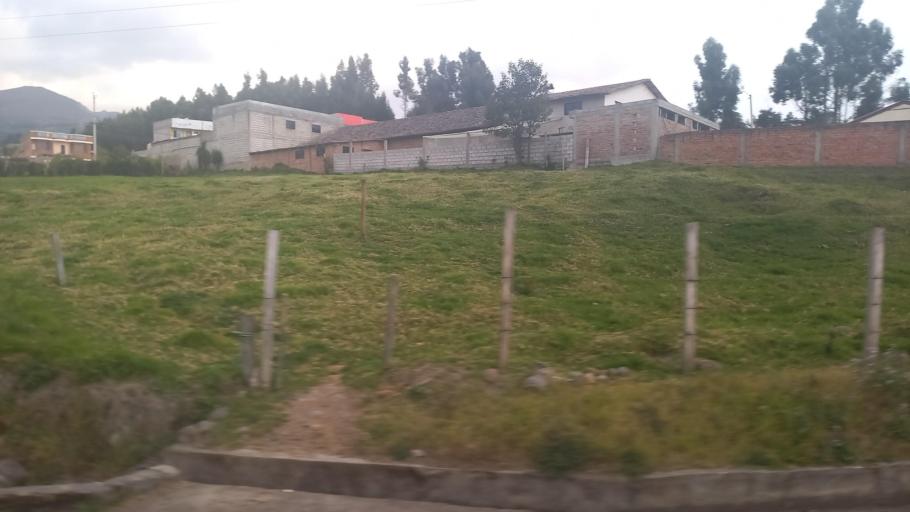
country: EC
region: Pichincha
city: Cayambe
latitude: 0.0910
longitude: -78.1002
